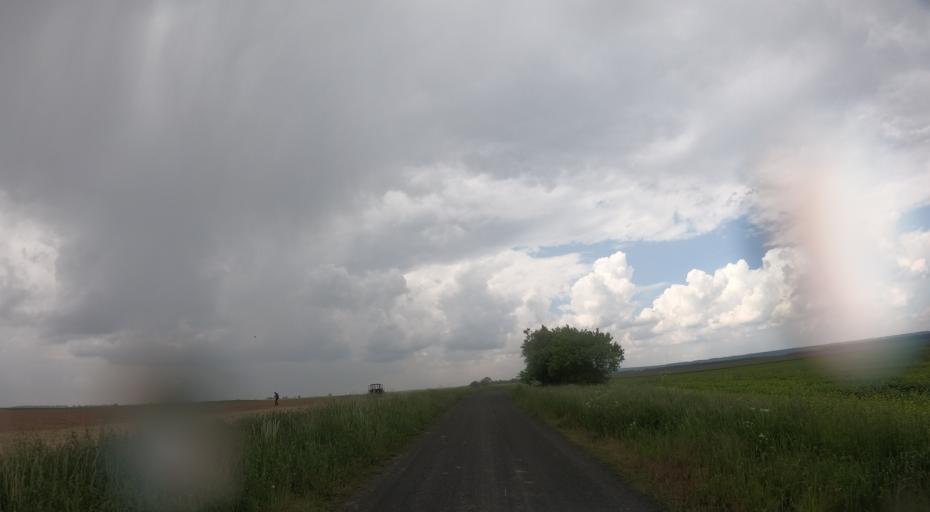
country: PL
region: West Pomeranian Voivodeship
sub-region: Powiat pyrzycki
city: Bielice
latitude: 53.2547
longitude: 14.7111
